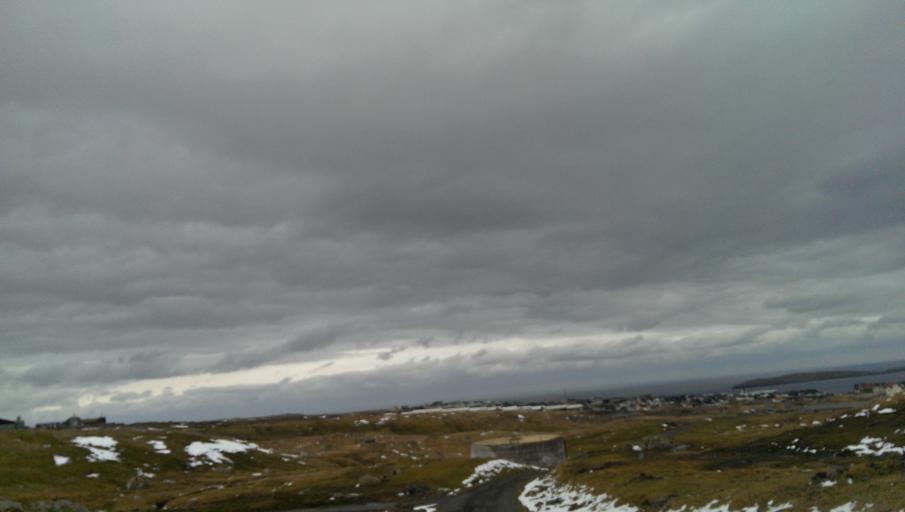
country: FO
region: Streymoy
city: Hoyvik
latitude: 62.0334
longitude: -6.8065
